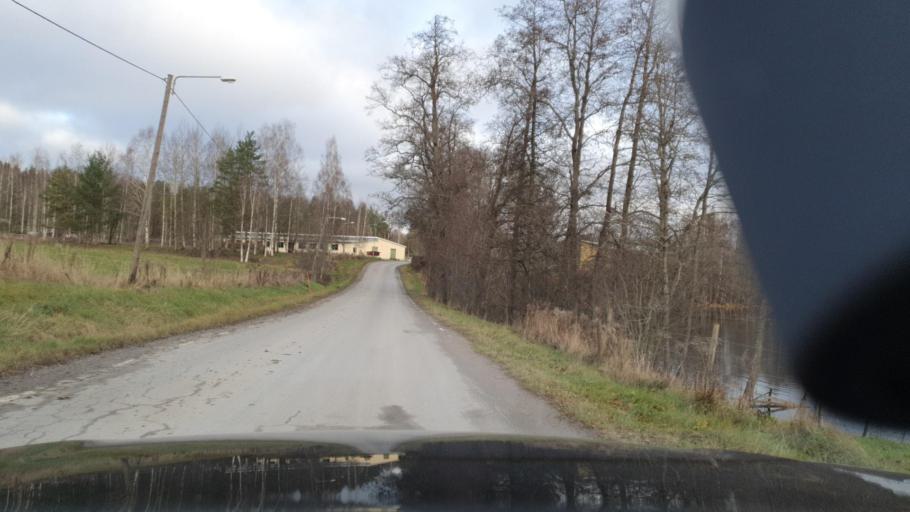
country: SE
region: Vaermland
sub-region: Arvika Kommun
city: Arvika
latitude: 59.7582
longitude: 12.5404
